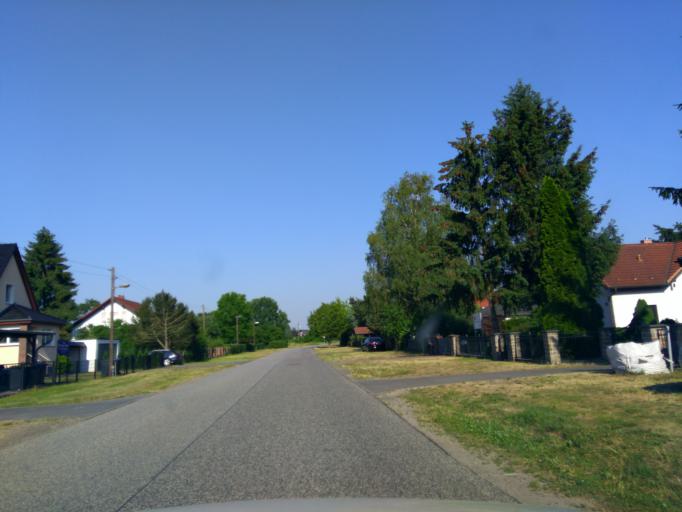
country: DE
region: Brandenburg
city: Brieselang
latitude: 52.5605
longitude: 13.0259
